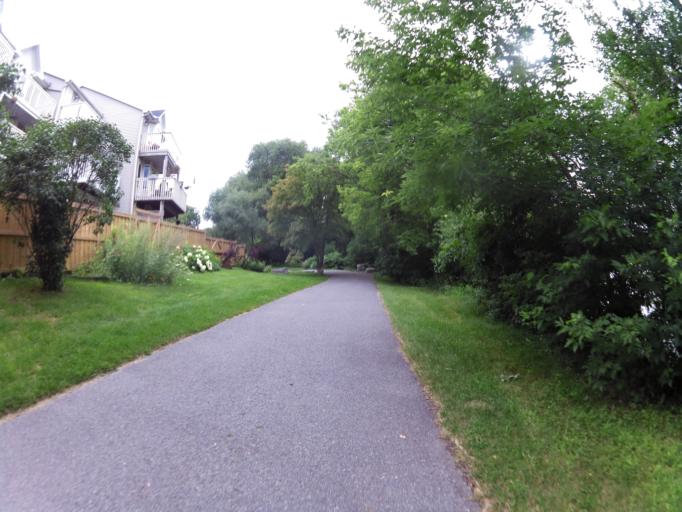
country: CA
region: Ontario
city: Ottawa
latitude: 45.4191
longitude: -75.6654
